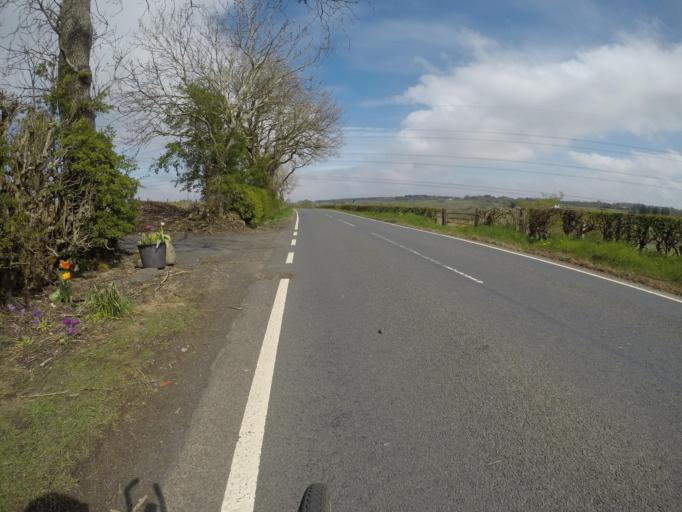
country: GB
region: Scotland
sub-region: East Ayrshire
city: Stewarton
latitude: 55.7039
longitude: -4.4712
